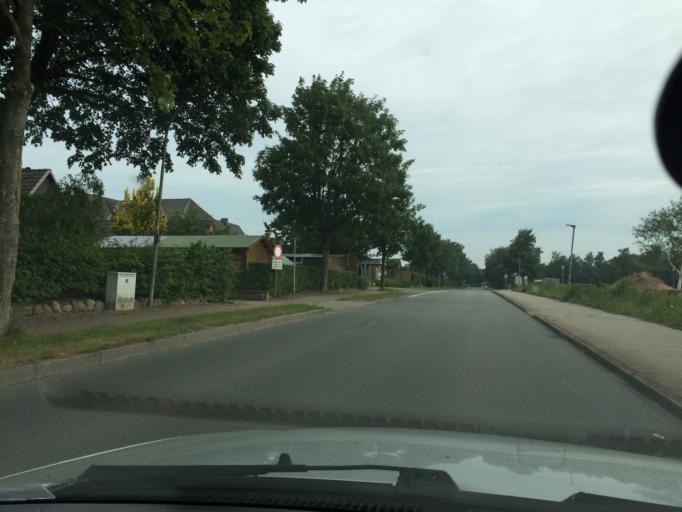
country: DE
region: Schleswig-Holstein
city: Oeversee
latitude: 54.6981
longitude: 9.4285
